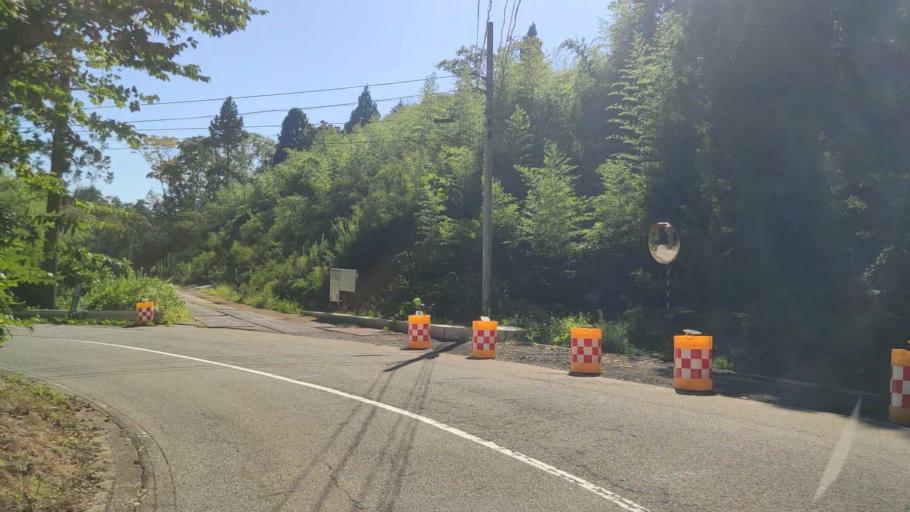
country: JP
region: Ishikawa
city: Nanao
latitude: 37.5101
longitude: 137.3367
